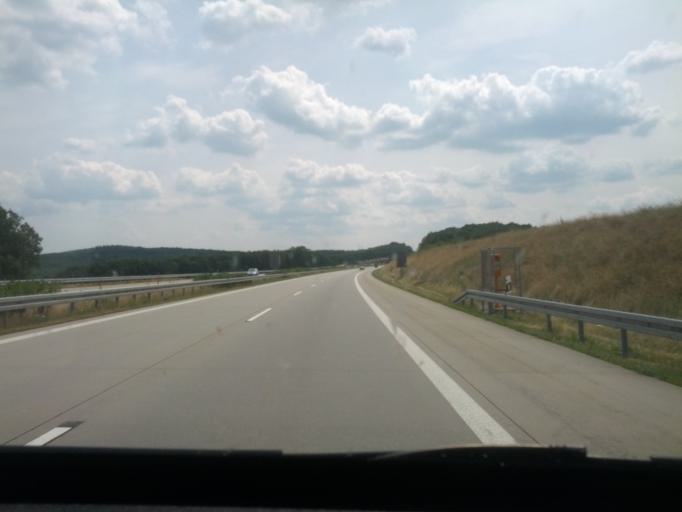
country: DE
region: Saxony
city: Liebstadt
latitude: 50.8502
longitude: 13.8798
